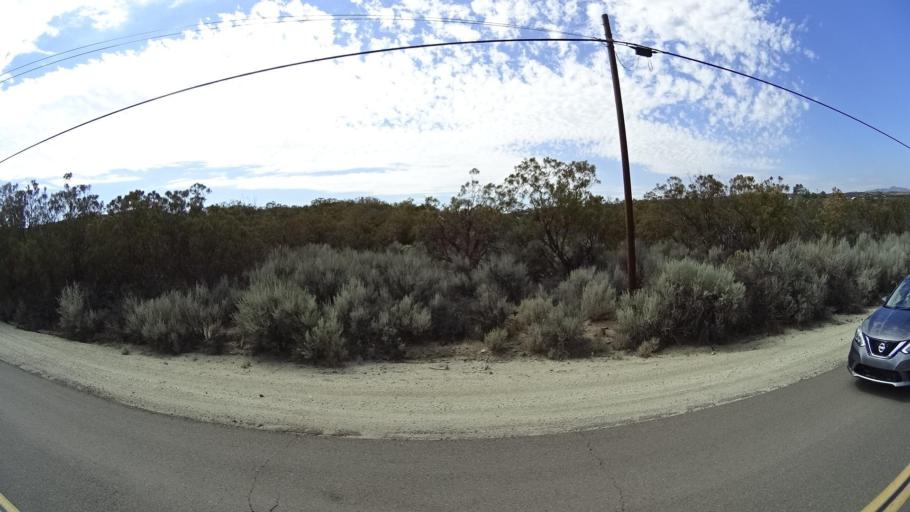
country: MX
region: Baja California
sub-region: Tecate
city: Cereso del Hongo
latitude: 32.6662
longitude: -116.2902
